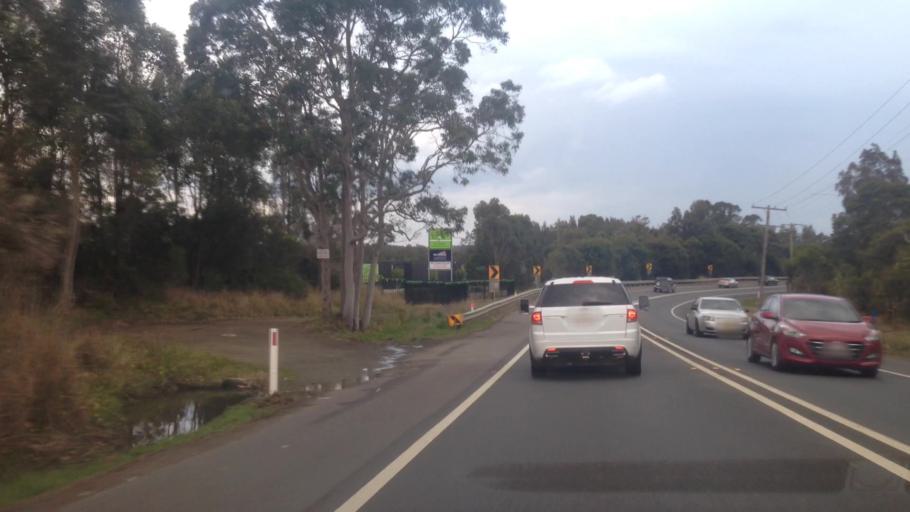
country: AU
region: New South Wales
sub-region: Wyong Shire
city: Tuggerawong
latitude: -33.2635
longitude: 151.4555
